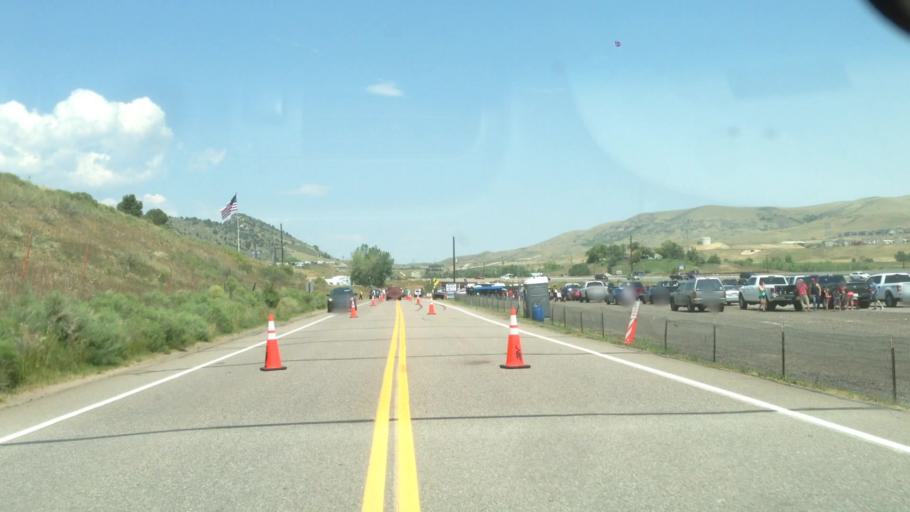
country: US
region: Colorado
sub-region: Jefferson County
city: Indian Hills
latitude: 39.6584
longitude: -105.1839
